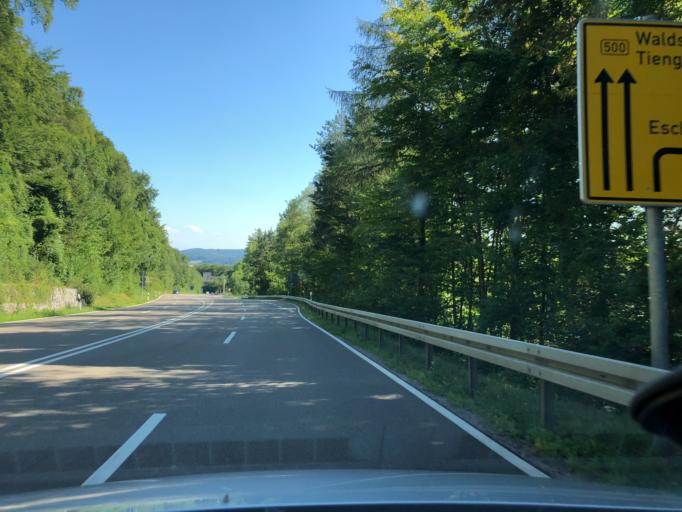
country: DE
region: Baden-Wuerttemberg
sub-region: Freiburg Region
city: Dogern
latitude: 47.6287
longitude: 8.1841
